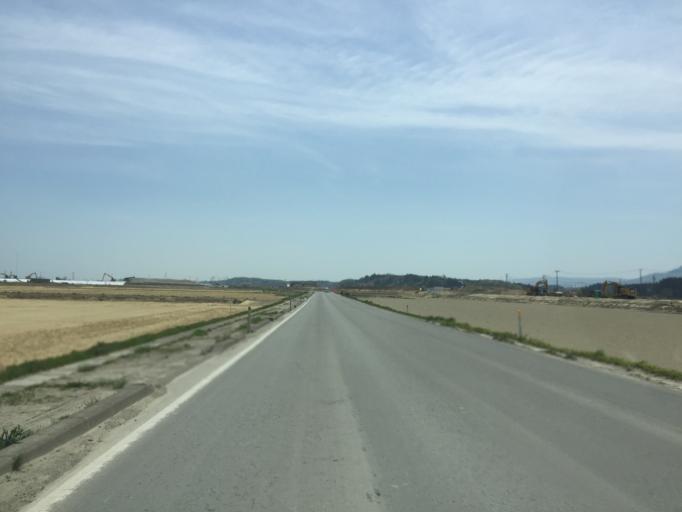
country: JP
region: Miyagi
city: Watari
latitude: 37.9312
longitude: 140.9131
